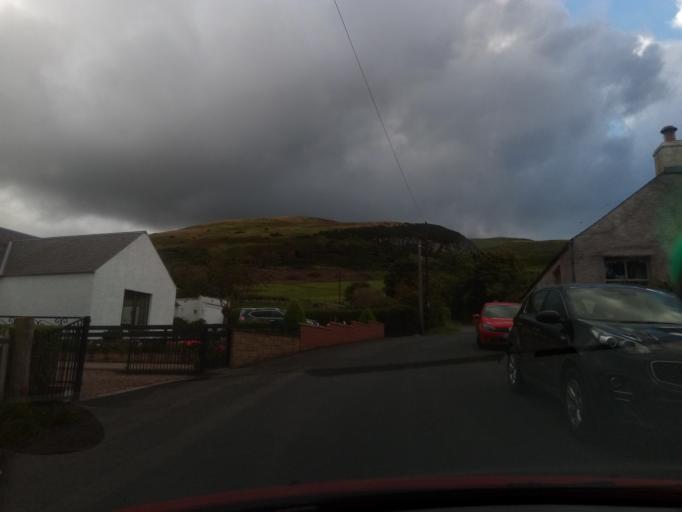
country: GB
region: Scotland
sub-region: The Scottish Borders
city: Coldstream
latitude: 55.5465
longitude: -2.2743
